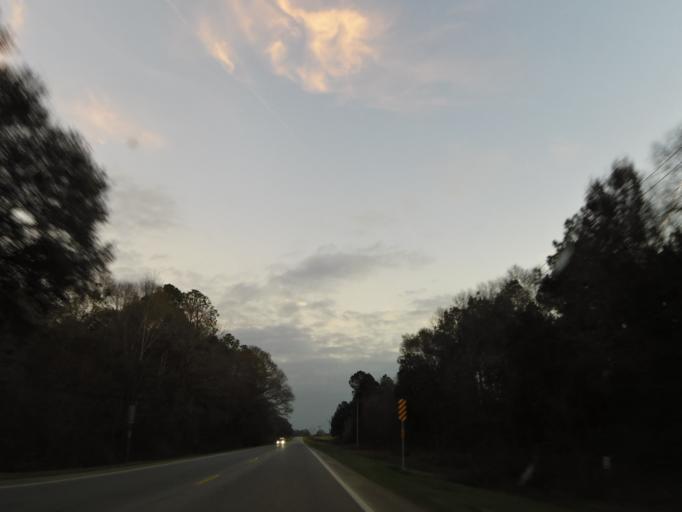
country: US
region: Georgia
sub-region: Dougherty County
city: Putney
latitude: 31.4906
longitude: -84.0287
